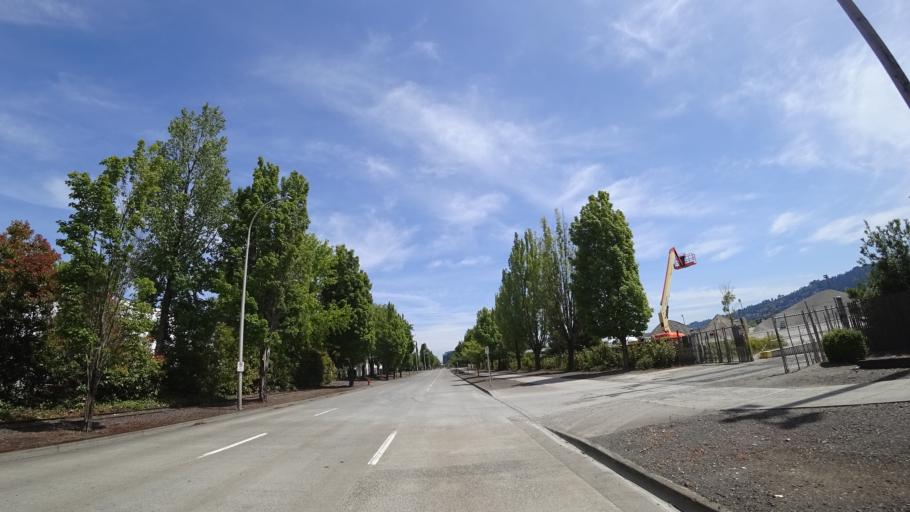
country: US
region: Oregon
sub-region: Multnomah County
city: Portland
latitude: 45.5613
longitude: -122.7136
